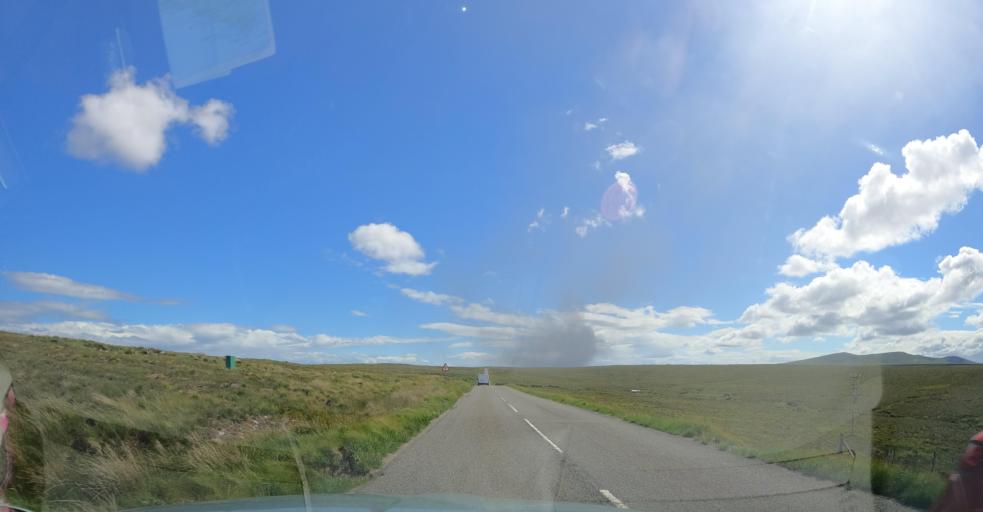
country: GB
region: Scotland
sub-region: Eilean Siar
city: Isle of Lewis
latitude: 58.3012
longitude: -6.4488
